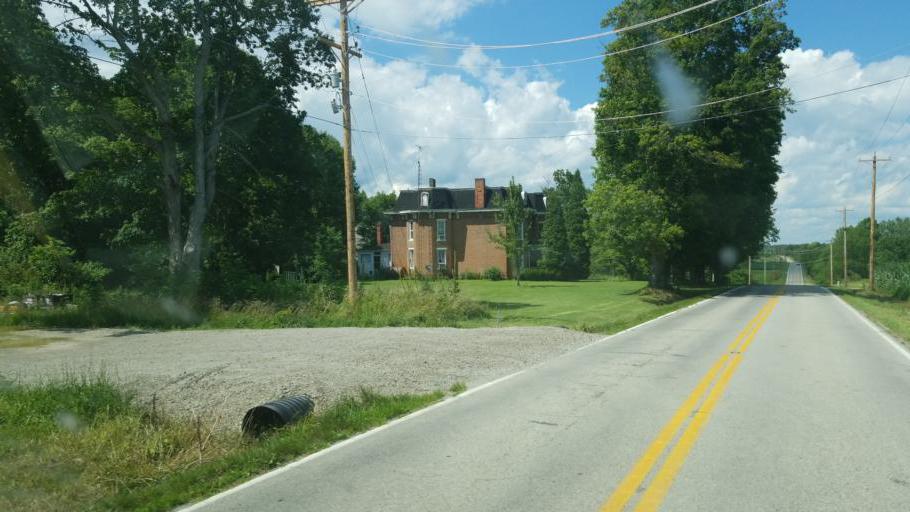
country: US
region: Ohio
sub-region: Highland County
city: Greenfield
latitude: 39.3184
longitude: -83.4055
